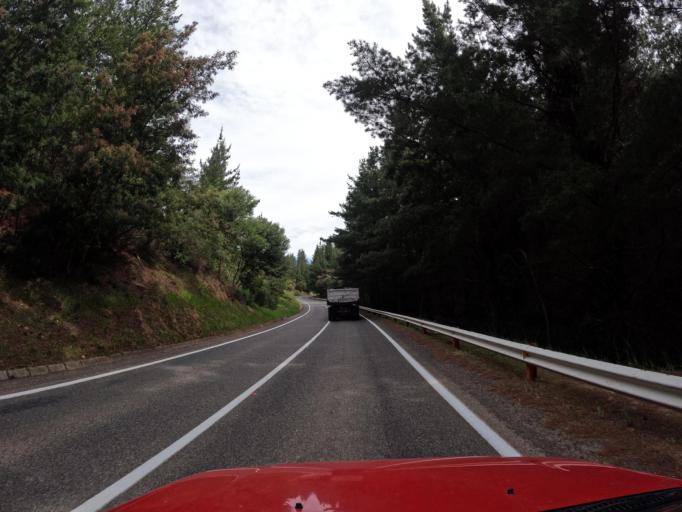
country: CL
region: Maule
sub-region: Provincia de Talca
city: Talca
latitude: -35.2892
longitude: -71.9755
